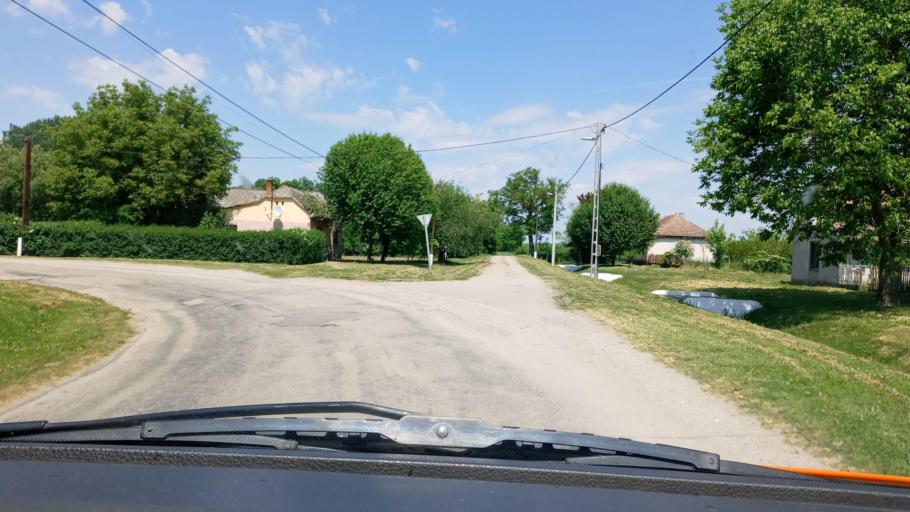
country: HR
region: Osjecko-Baranjska
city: Viljevo
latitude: 45.8160
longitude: 18.1189
